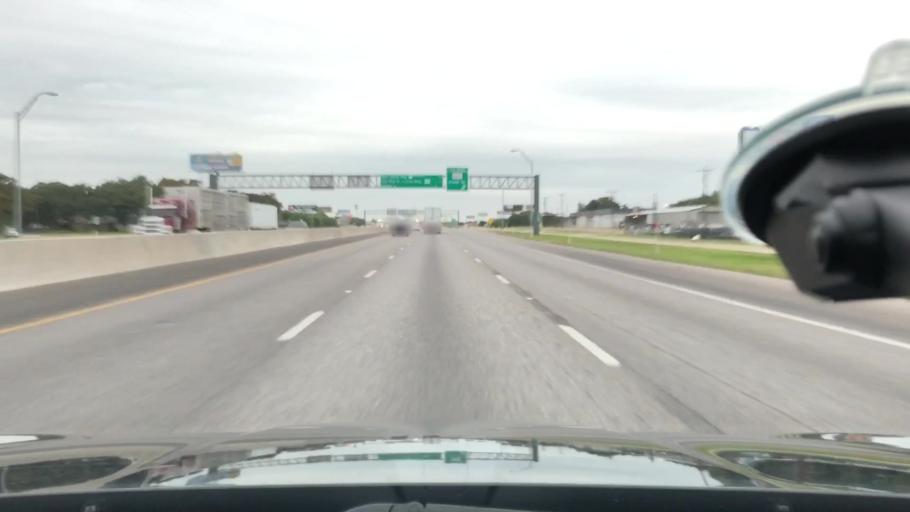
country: US
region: Texas
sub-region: McLennan County
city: Northcrest
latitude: 31.6307
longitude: -97.0955
